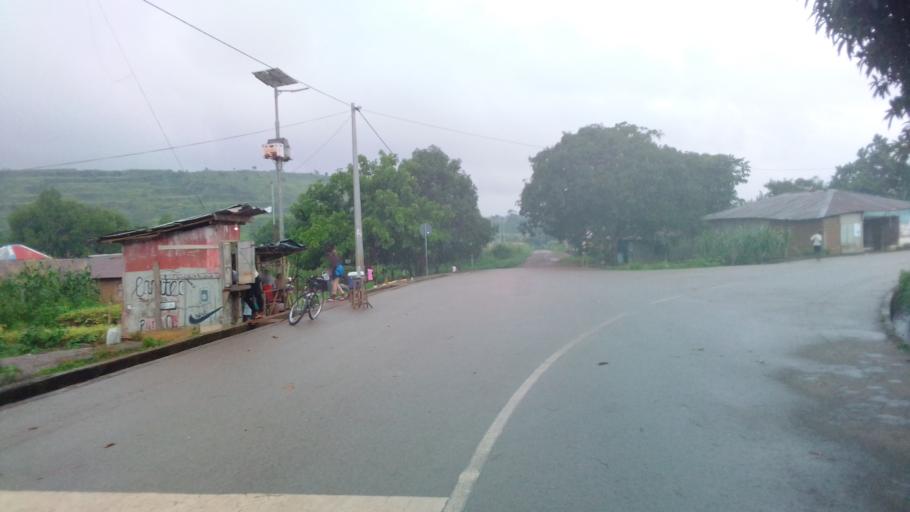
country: SL
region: Northern Province
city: Lunsar
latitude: 8.6834
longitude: -12.5286
